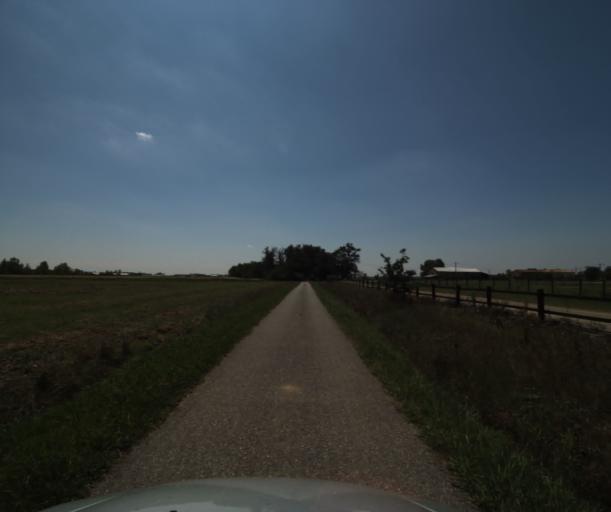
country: FR
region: Midi-Pyrenees
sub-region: Departement de la Haute-Garonne
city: Labastidette
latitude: 43.4573
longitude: 1.2660
